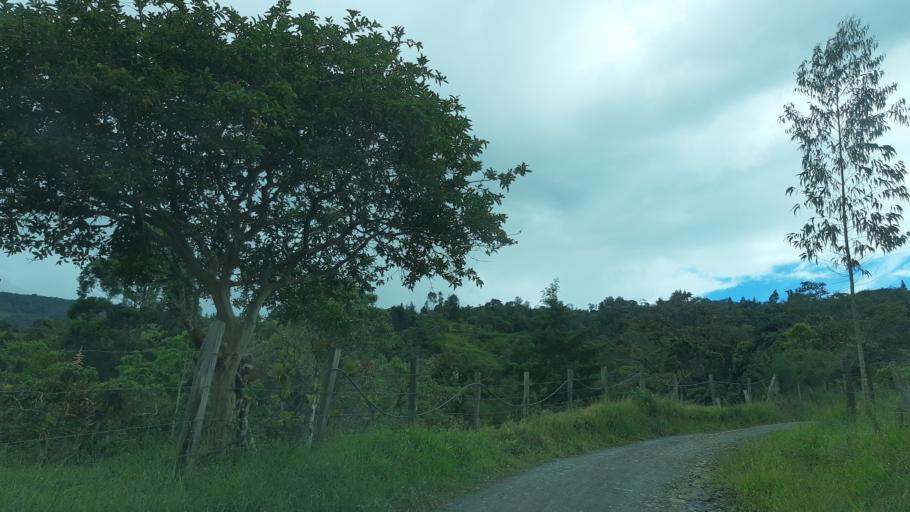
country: CO
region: Boyaca
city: Garagoa
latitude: 5.0198
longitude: -73.3324
